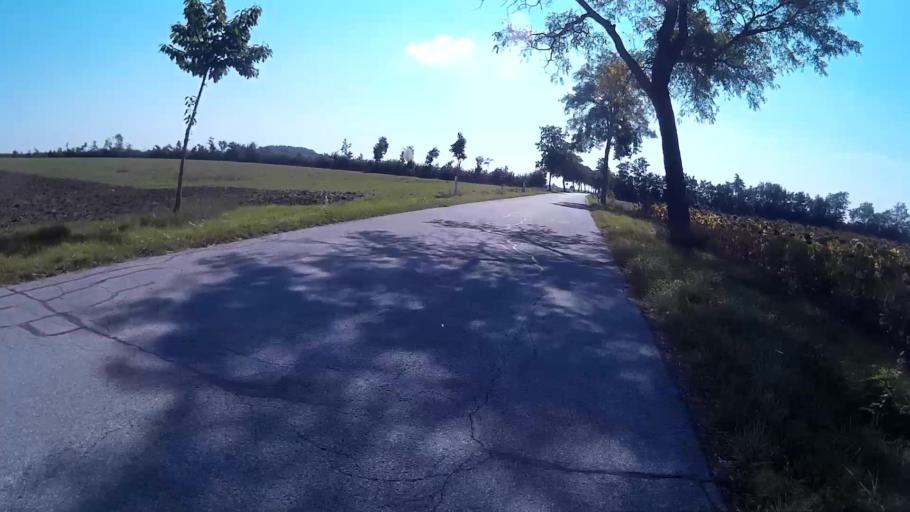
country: CZ
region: South Moravian
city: Novosedly
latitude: 48.7799
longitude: 16.4934
